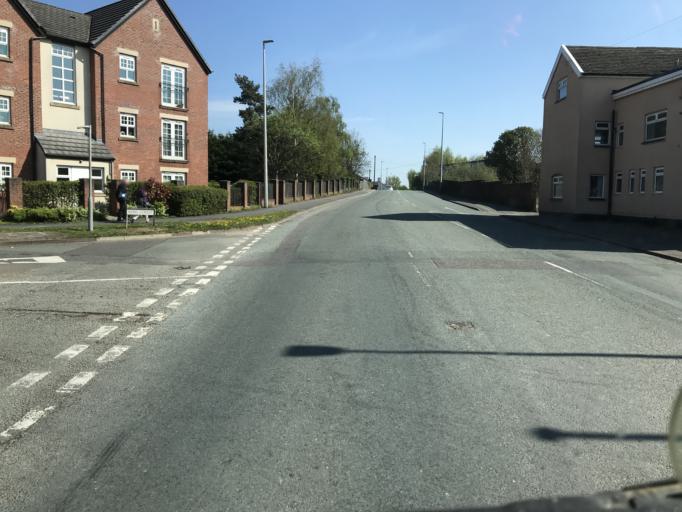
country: GB
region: England
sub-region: Cheshire East
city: Middlewich
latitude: 53.1933
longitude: -2.4412
